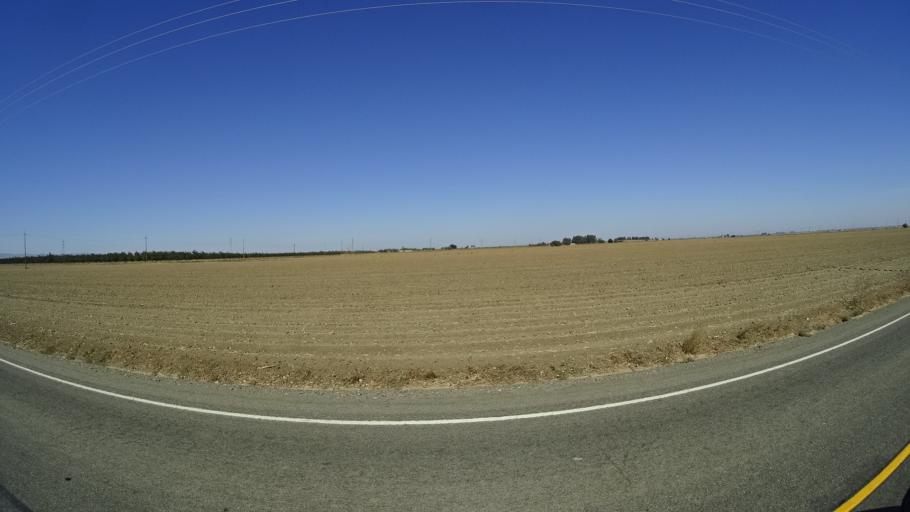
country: US
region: California
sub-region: Yolo County
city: Cottonwood
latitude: 38.6203
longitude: -121.9602
